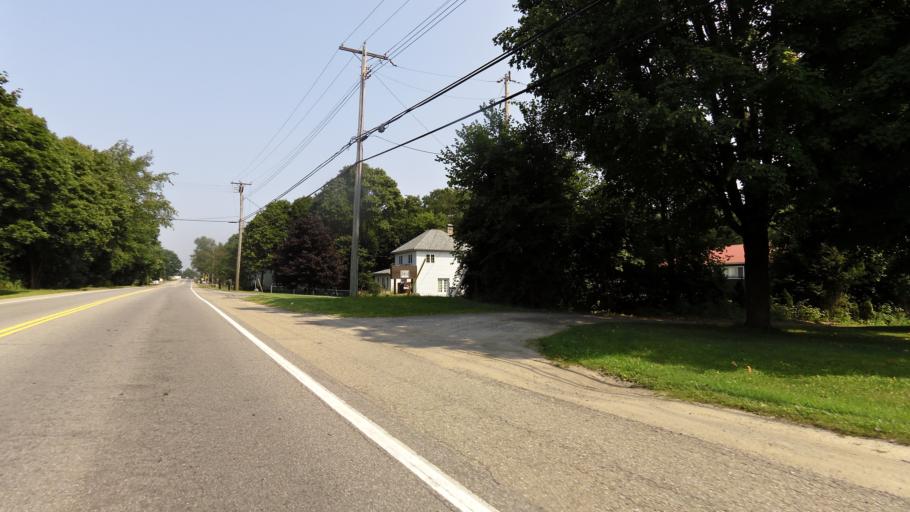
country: CA
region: Ontario
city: Brockville
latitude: 44.6048
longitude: -75.6616
